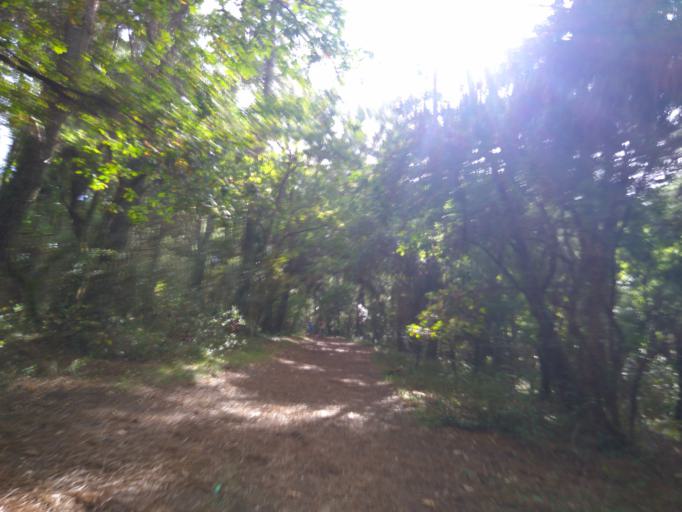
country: FR
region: Aquitaine
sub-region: Departement des Landes
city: Capbreton
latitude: 43.6316
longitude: -1.4423
